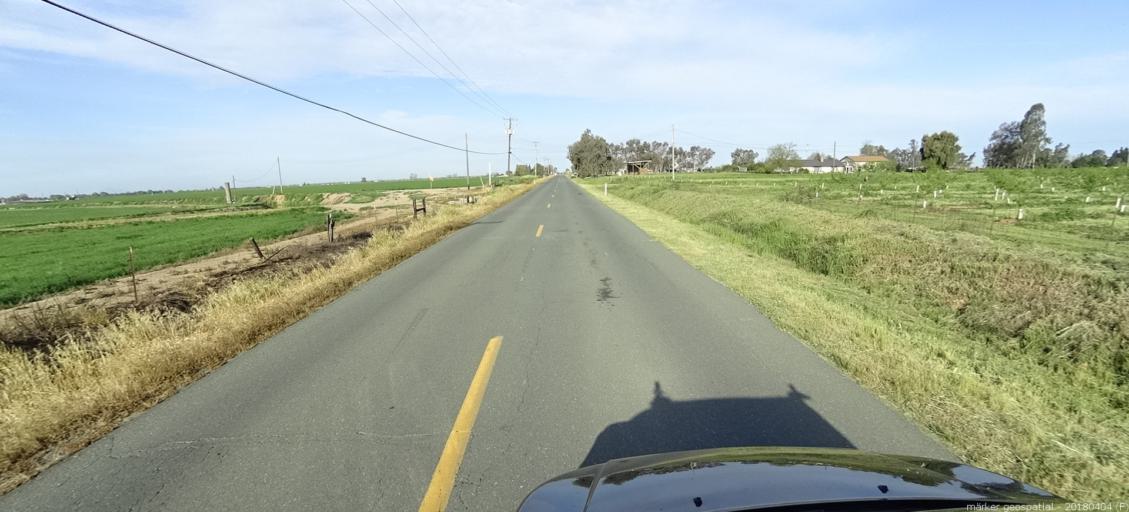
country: US
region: California
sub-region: Sacramento County
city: Herald
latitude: 38.3257
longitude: -121.2917
